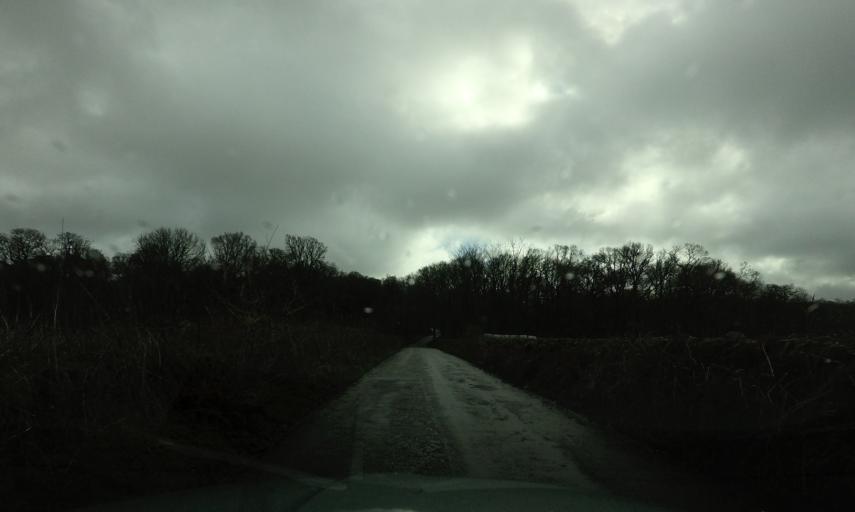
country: GB
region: Scotland
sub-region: West Dunbartonshire
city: Balloch
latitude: 56.1113
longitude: -4.5790
